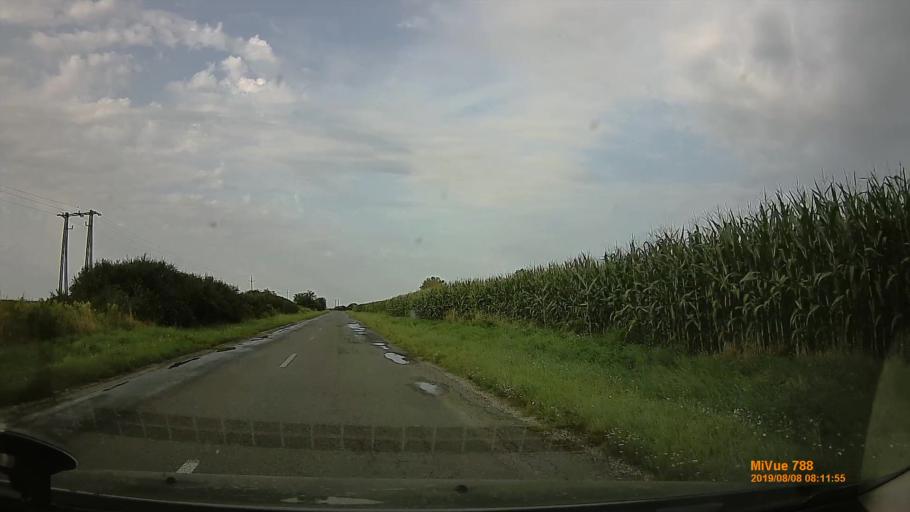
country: HU
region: Zala
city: Murakeresztur
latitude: 46.4186
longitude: 16.8768
